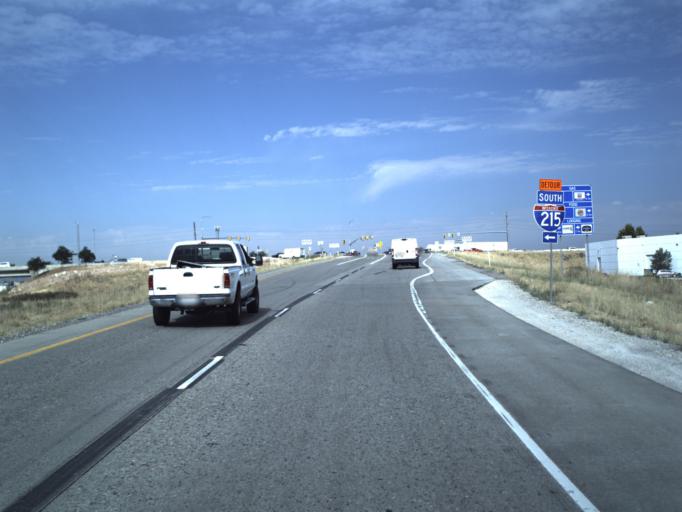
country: US
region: Utah
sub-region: Salt Lake County
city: West Valley City
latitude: 40.7263
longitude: -111.9831
